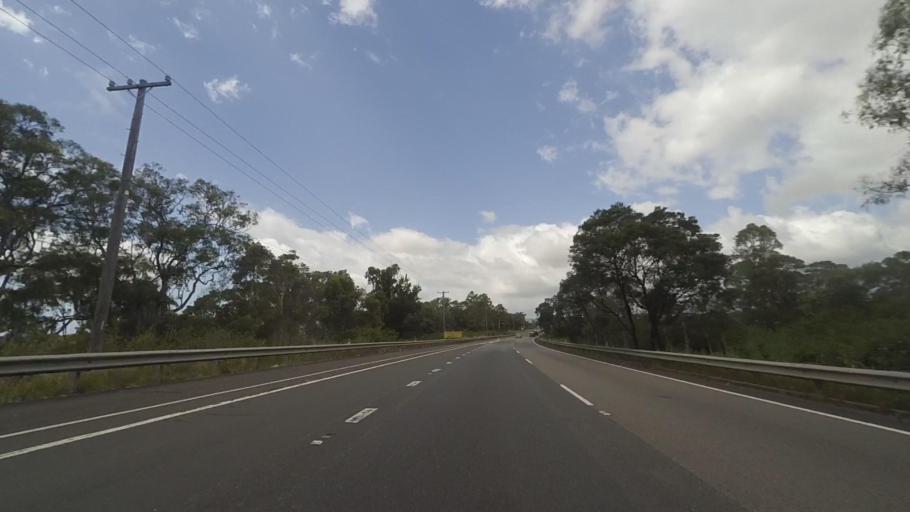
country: AU
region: New South Wales
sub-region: Shellharbour
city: Albion Park Rail
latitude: -34.5324
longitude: 150.7871
